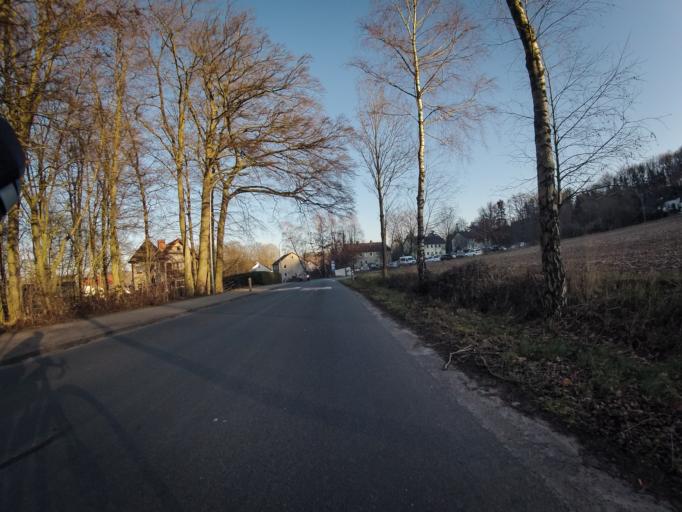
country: DE
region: Lower Saxony
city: Wallenhorst
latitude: 52.3259
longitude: 8.0237
